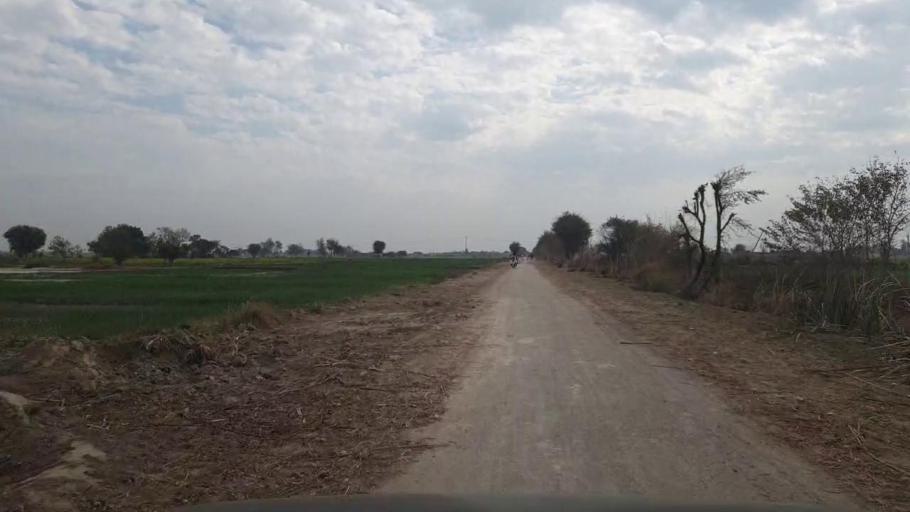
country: PK
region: Sindh
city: Sakrand
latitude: 26.0164
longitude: 68.4306
